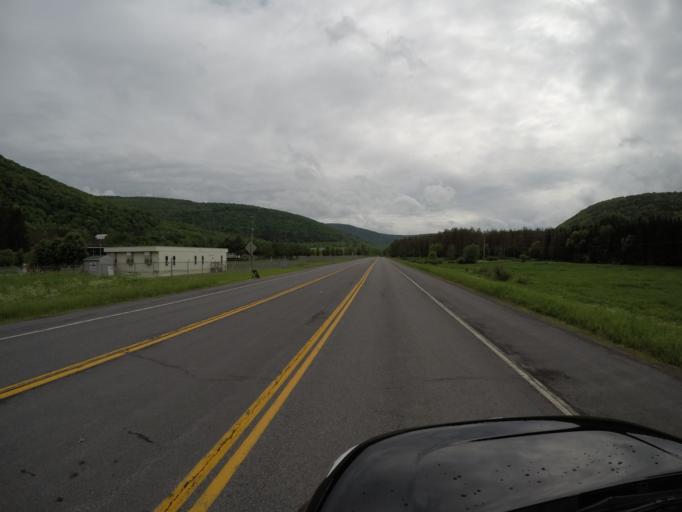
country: US
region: New York
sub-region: Delaware County
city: Stamford
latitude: 42.1417
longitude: -74.6534
